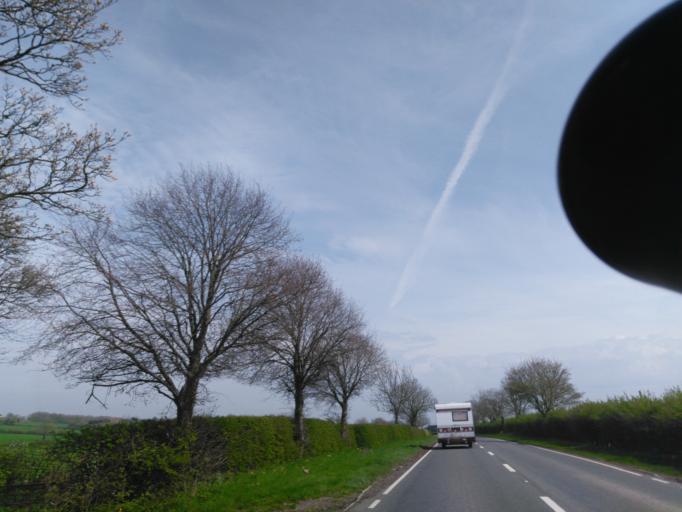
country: GB
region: England
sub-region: Somerset
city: Shepton Mallet
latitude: 51.1699
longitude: -2.5650
